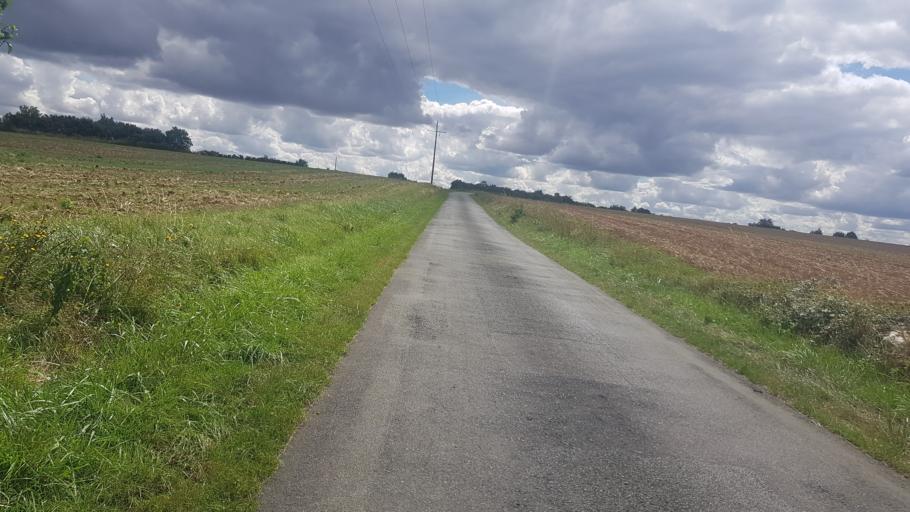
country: FR
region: Poitou-Charentes
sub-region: Departement des Deux-Sevres
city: Vouille
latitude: 46.3229
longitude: -0.3441
